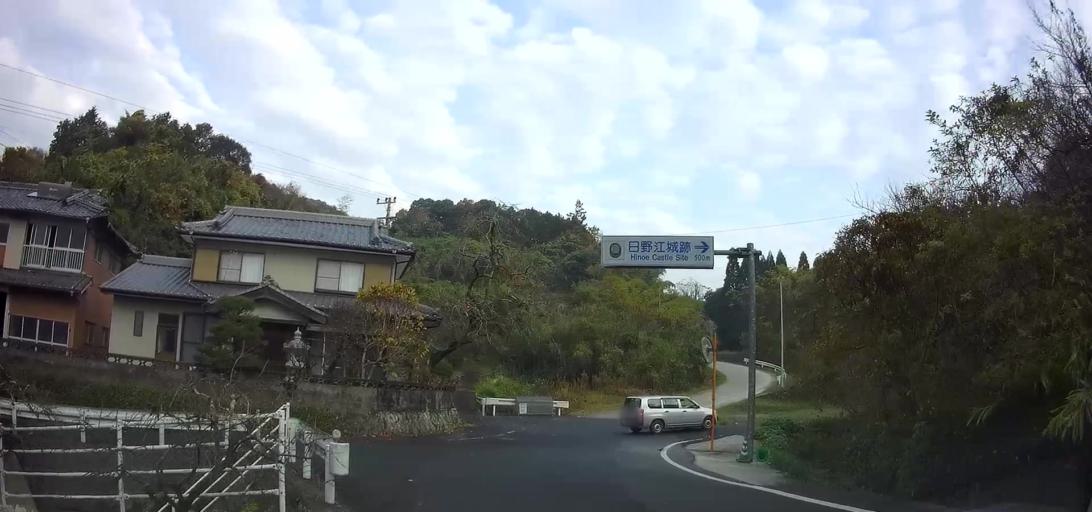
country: JP
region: Nagasaki
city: Shimabara
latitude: 32.6594
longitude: 130.2494
